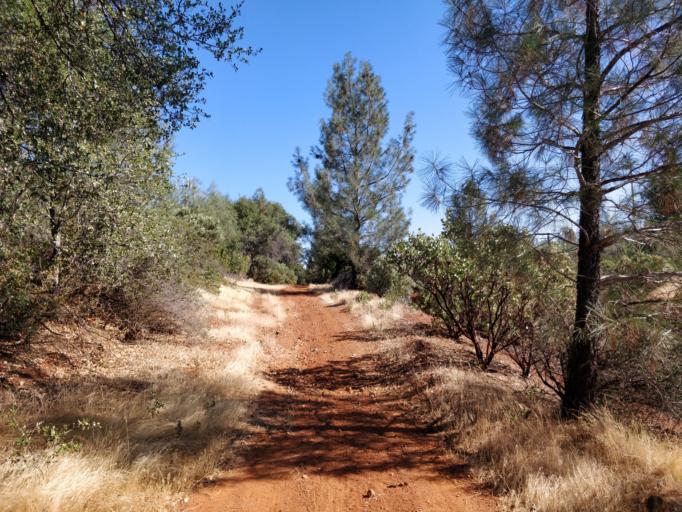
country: US
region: California
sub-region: Shasta County
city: Central Valley (historical)
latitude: 40.6646
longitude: -122.3941
